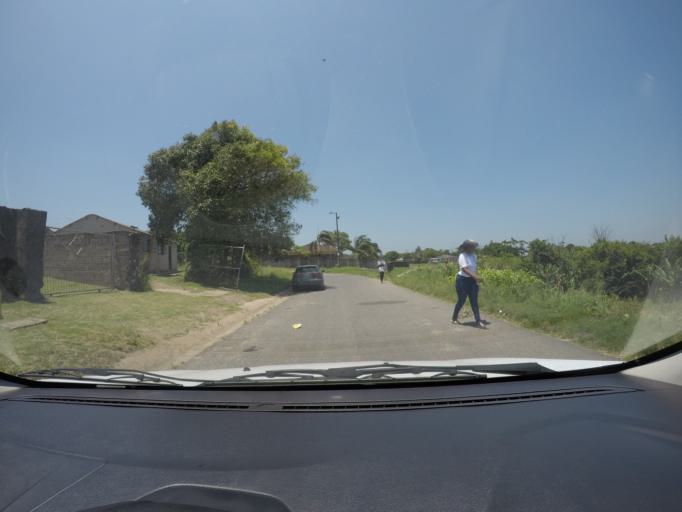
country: ZA
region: KwaZulu-Natal
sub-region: uThungulu District Municipality
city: eSikhawini
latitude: -28.8800
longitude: 31.9060
